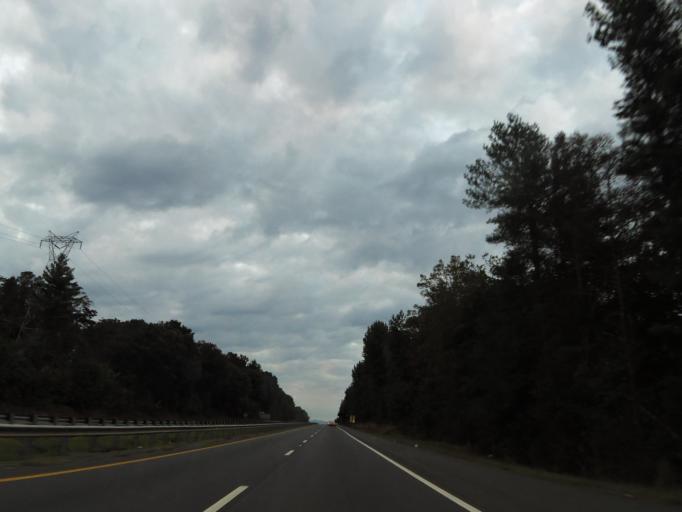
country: US
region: North Carolina
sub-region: Buncombe County
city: Weaverville
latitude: 35.6759
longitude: -82.5832
